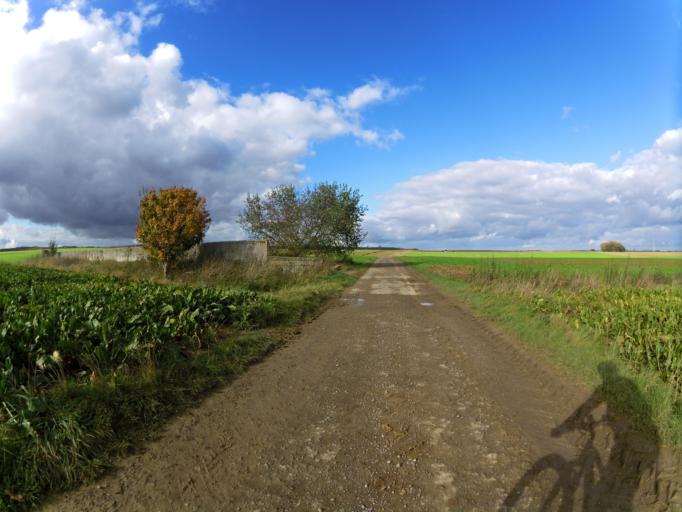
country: DE
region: Bavaria
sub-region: Regierungsbezirk Unterfranken
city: Unterpleichfeld
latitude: 49.8751
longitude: 10.0180
